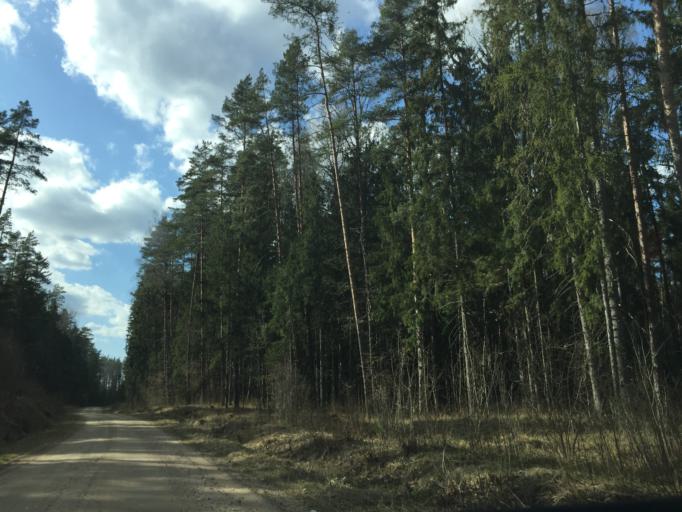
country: LV
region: Skriveri
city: Skriveri
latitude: 56.7838
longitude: 25.2255
